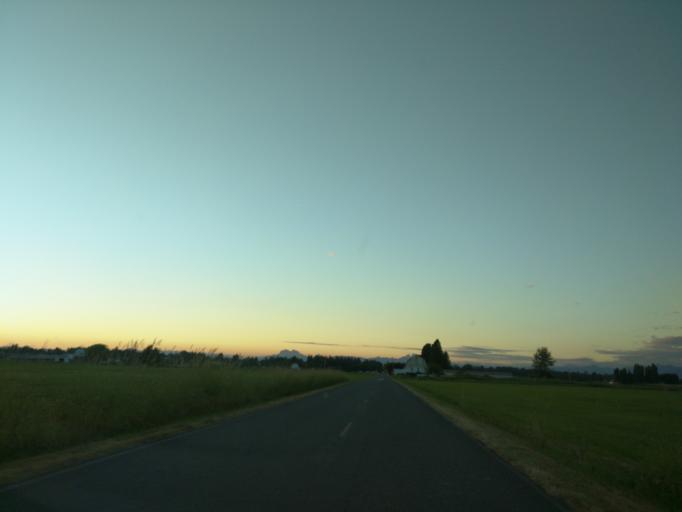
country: US
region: Washington
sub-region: Whatcom County
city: Lynden
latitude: 48.9384
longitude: -122.4081
